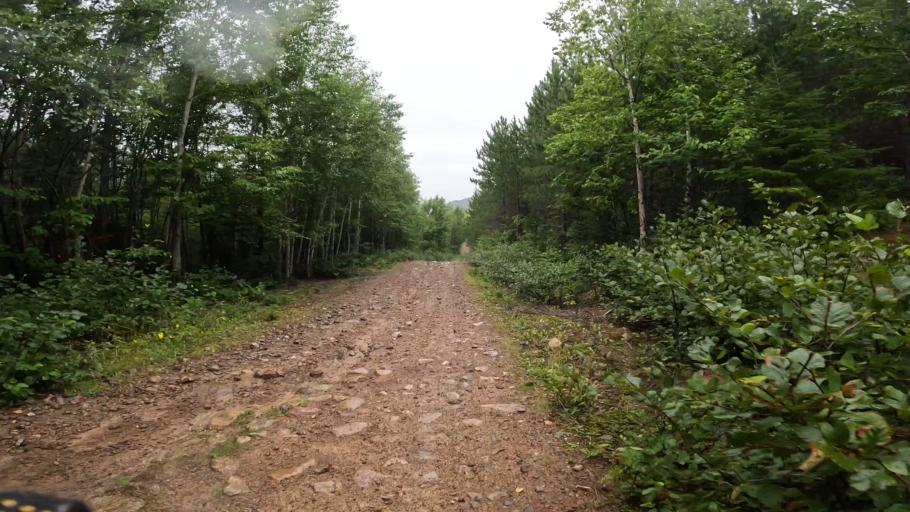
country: CA
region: Quebec
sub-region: Capitale-Nationale
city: Baie-Saint-Paul
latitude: 47.7927
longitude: -70.4882
